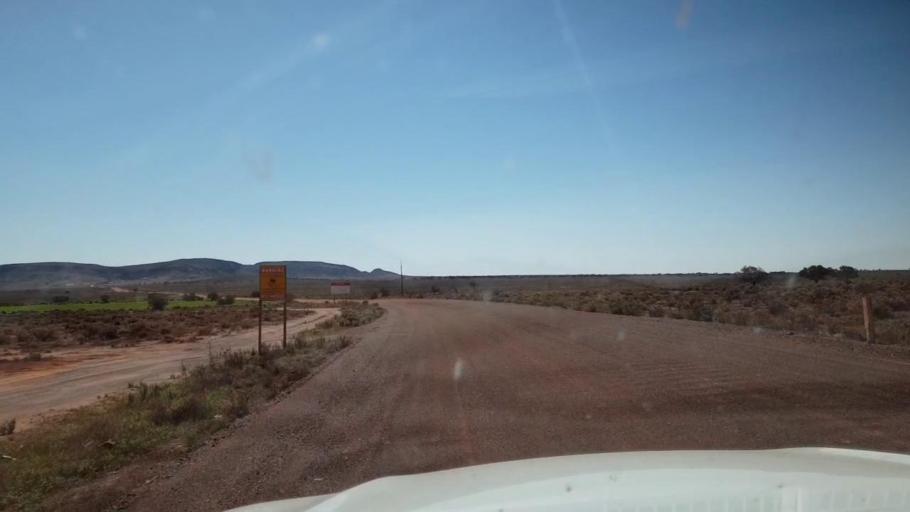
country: AU
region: South Australia
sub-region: Whyalla
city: Whyalla
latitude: -32.7175
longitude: 137.1434
